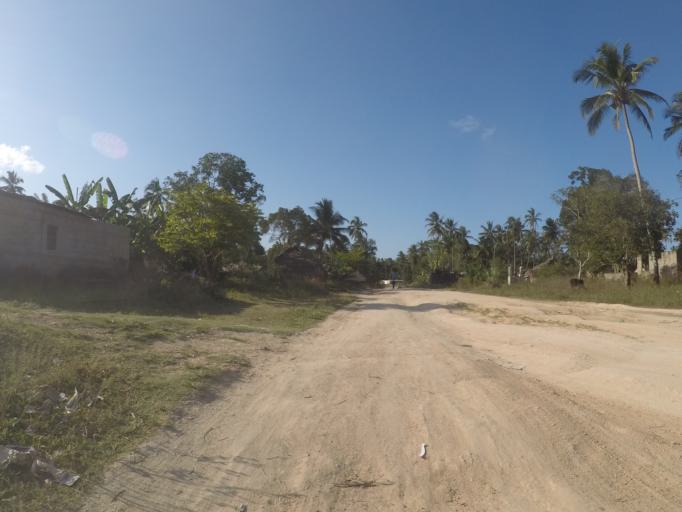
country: TZ
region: Zanzibar Central/South
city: Koani
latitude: -6.1543
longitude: 39.2875
